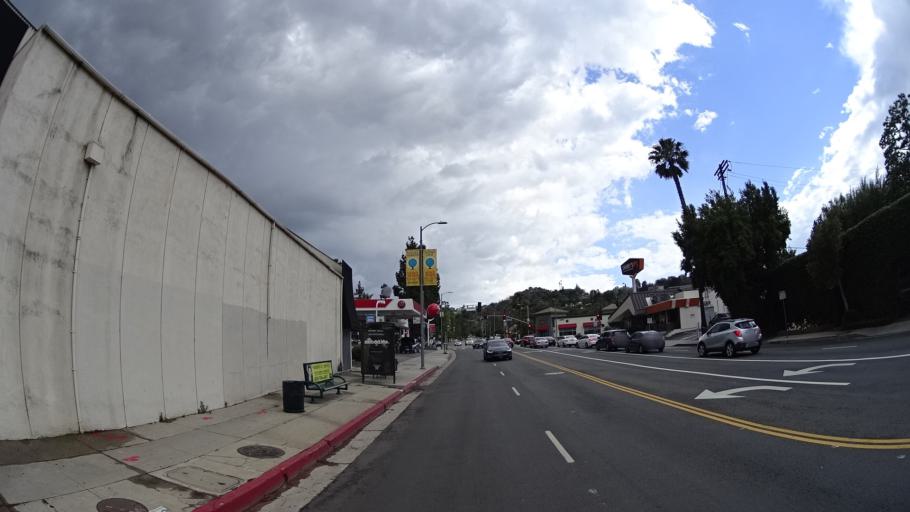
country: US
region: California
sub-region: Los Angeles County
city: Sherman Oaks
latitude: 34.1458
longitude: -118.4139
